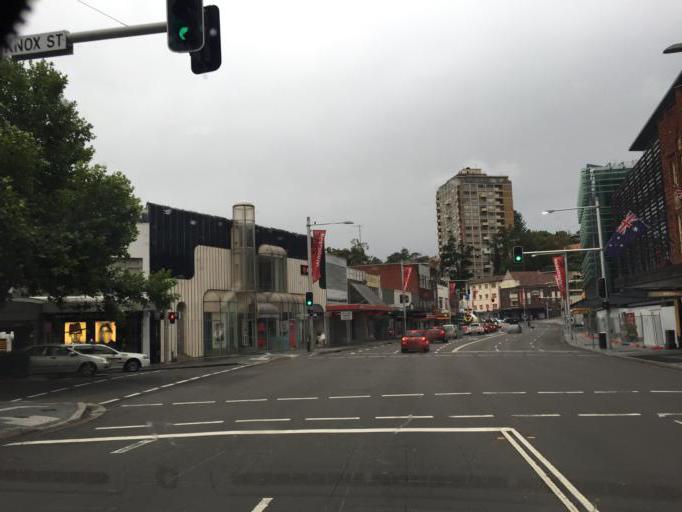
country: AU
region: New South Wales
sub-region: Woollahra
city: Bellevue Hill
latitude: -33.8776
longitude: 151.2432
